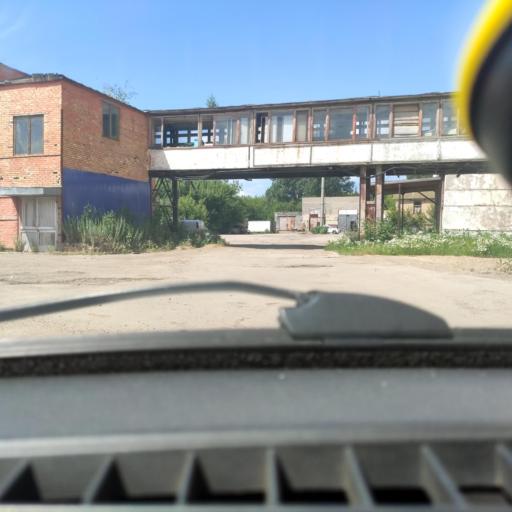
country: RU
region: Samara
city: Zhigulevsk
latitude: 53.5235
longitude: 49.4839
